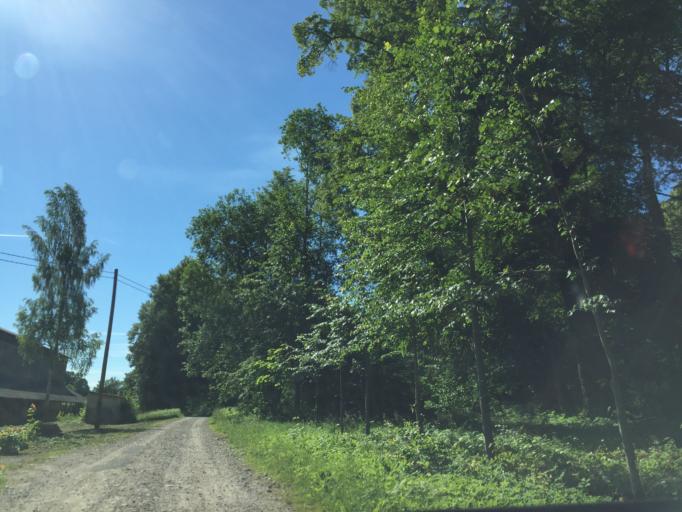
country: LV
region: Kuldigas Rajons
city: Kuldiga
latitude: 57.3226
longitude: 22.0413
